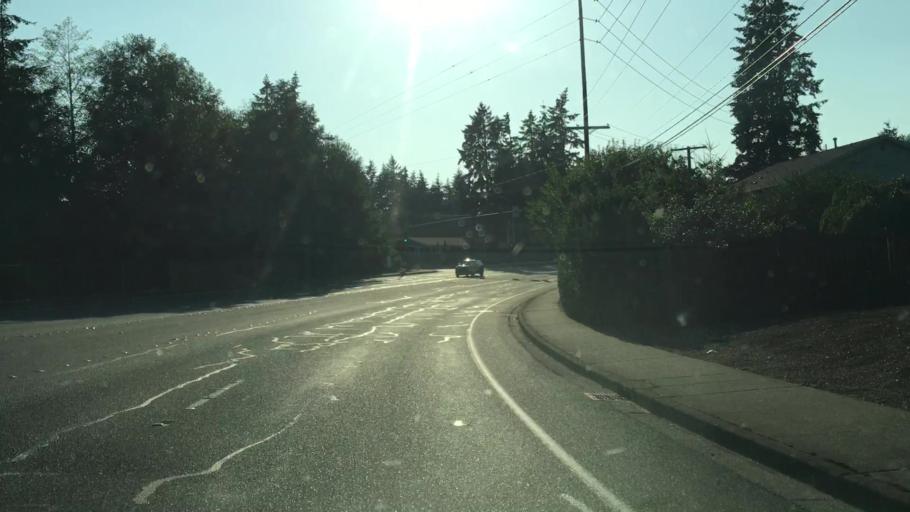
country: US
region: Washington
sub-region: Pierce County
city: Fife Heights
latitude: 47.2819
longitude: -122.3438
